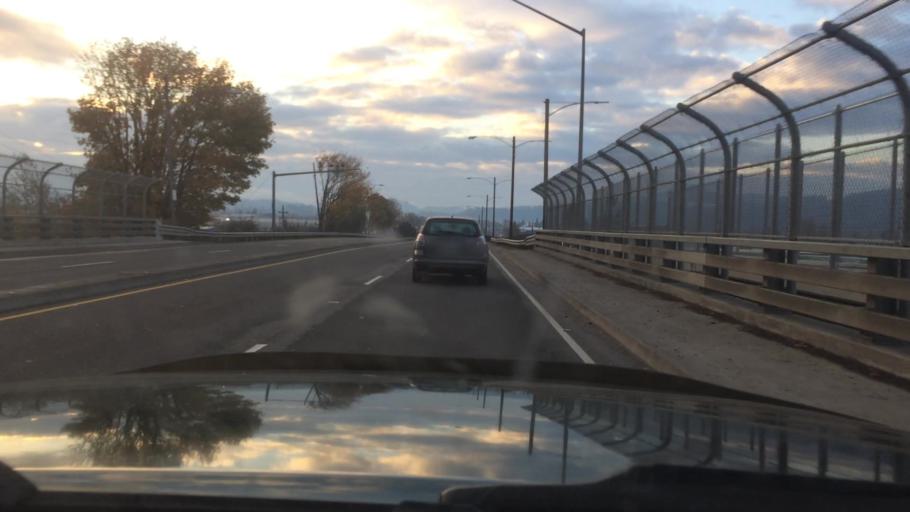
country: US
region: Oregon
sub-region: Lane County
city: Eugene
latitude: 44.0605
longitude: -123.1339
